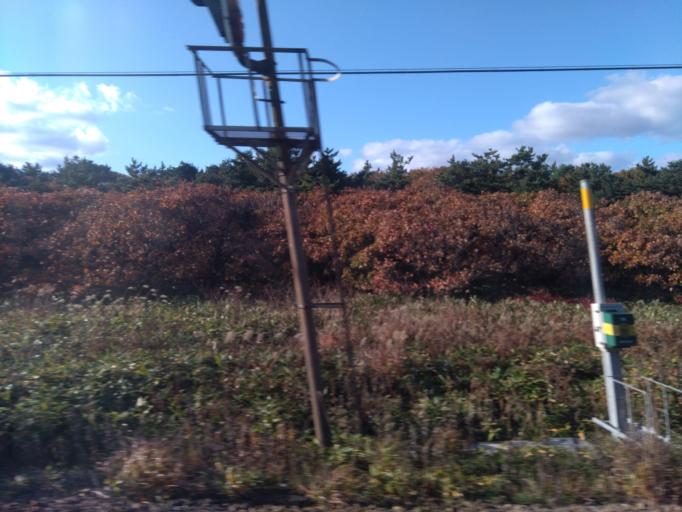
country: JP
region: Hokkaido
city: Niseko Town
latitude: 42.5544
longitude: 140.4224
